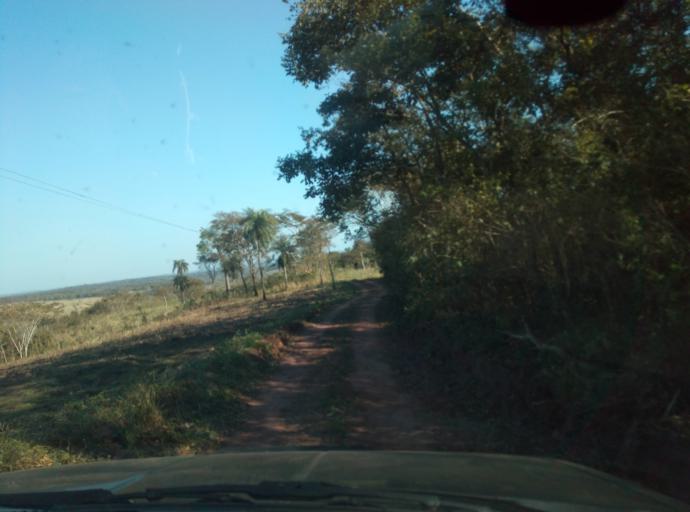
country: PY
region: Caaguazu
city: San Joaquin
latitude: -25.1684
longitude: -56.1163
